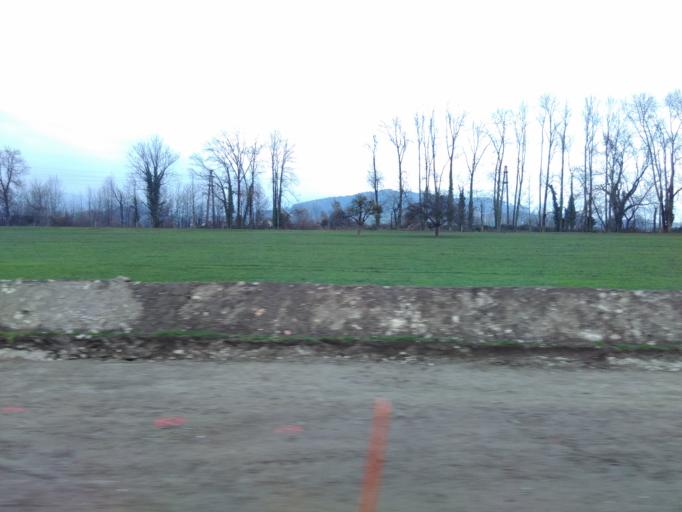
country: CH
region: Schwyz
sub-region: Bezirk March
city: Lachen
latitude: 47.1780
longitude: 8.8880
